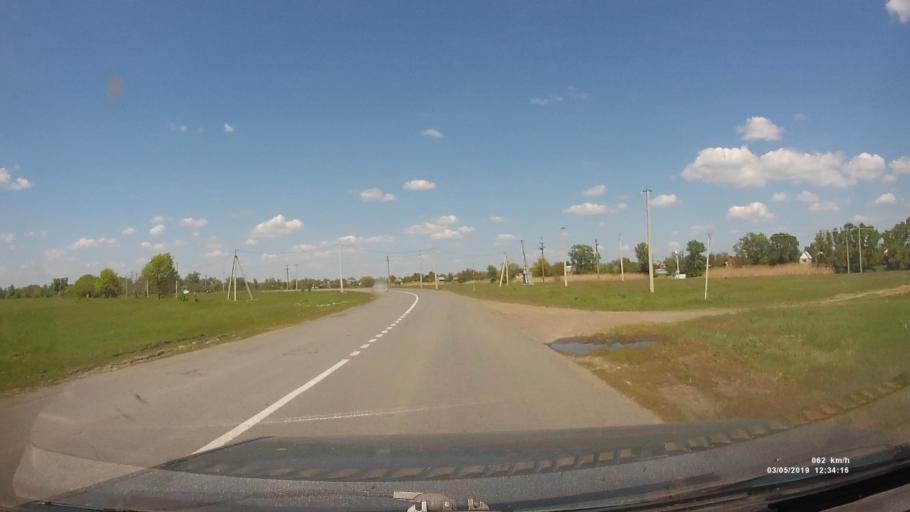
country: RU
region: Rostov
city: Semikarakorsk
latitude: 47.5210
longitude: 40.7688
